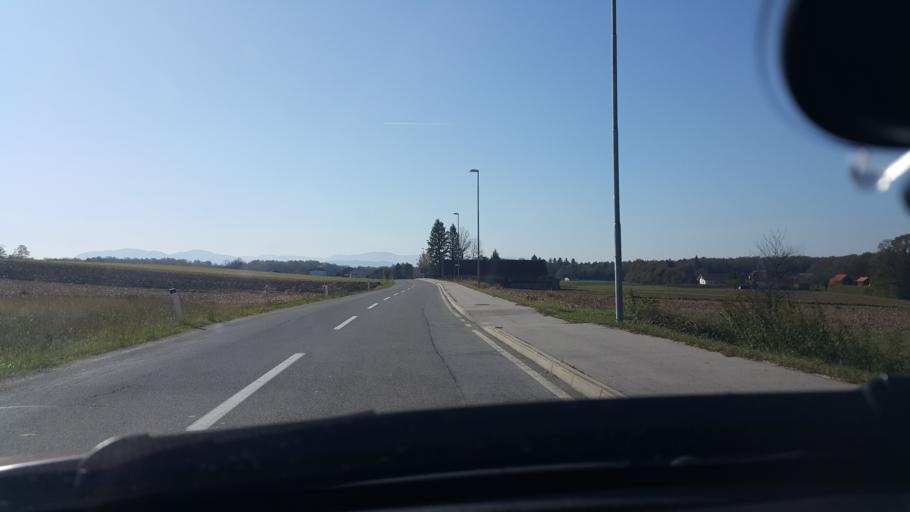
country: SI
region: Bistrica ob Sotli
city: Bistrica ob Sotli
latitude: 45.9577
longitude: 15.6825
